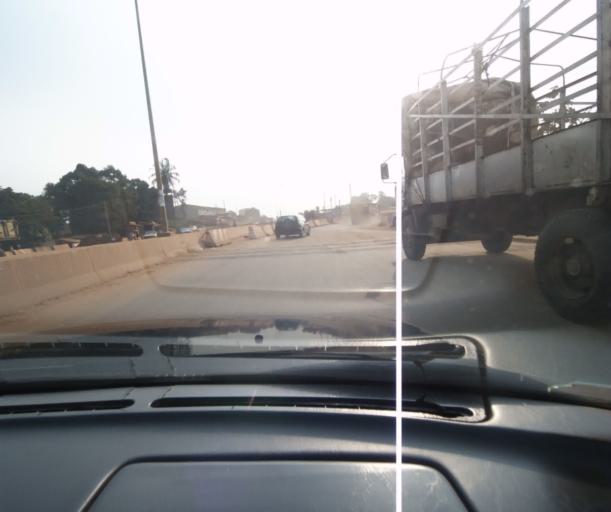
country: CM
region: Centre
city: Okoa
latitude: 3.9547
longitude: 11.5312
